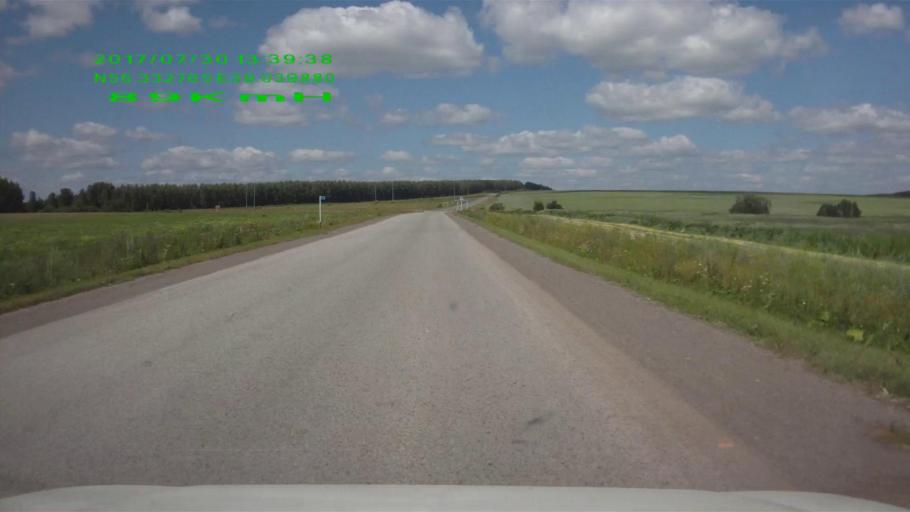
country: RU
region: Sverdlovsk
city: Mikhaylovsk
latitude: 56.3332
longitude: 59.0396
